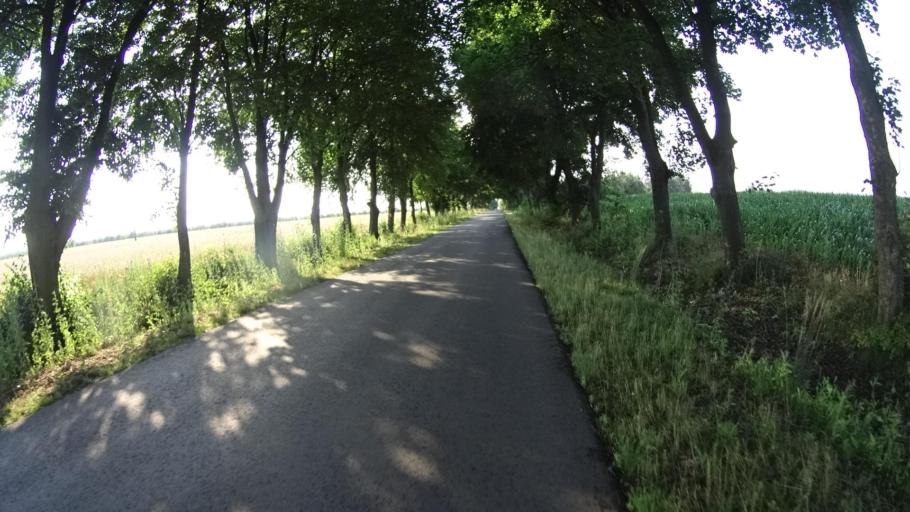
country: PL
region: Masovian Voivodeship
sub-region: Powiat grojecki
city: Goszczyn
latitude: 51.7061
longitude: 20.7969
